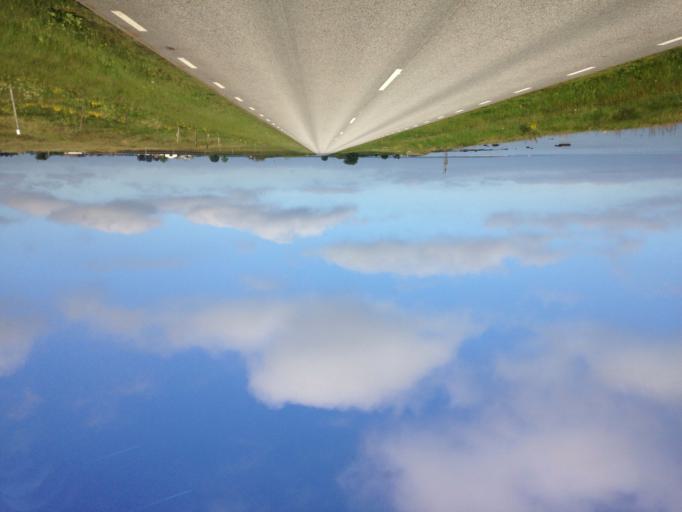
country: SE
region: Skane
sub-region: Trelleborgs Kommun
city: Skare
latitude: 55.3812
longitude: 13.0339
